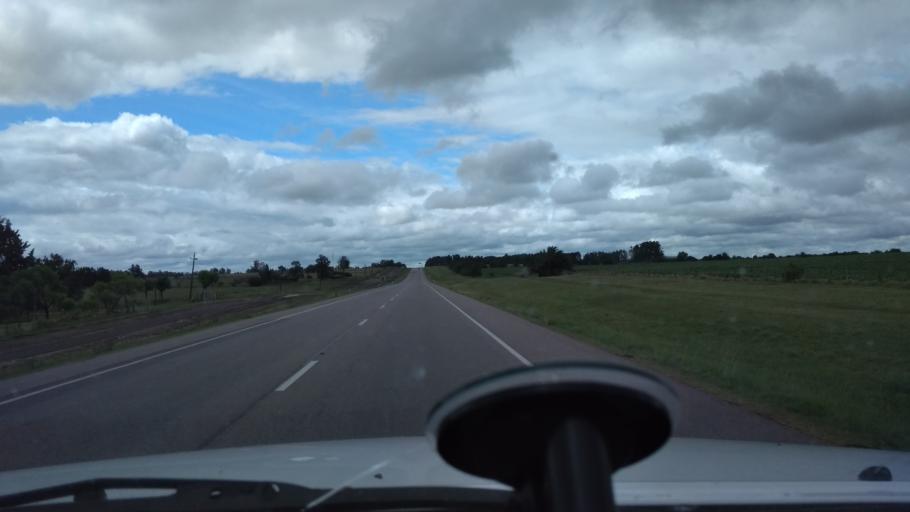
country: UY
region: Florida
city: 25 de Mayo
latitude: -34.2648
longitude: -56.2141
